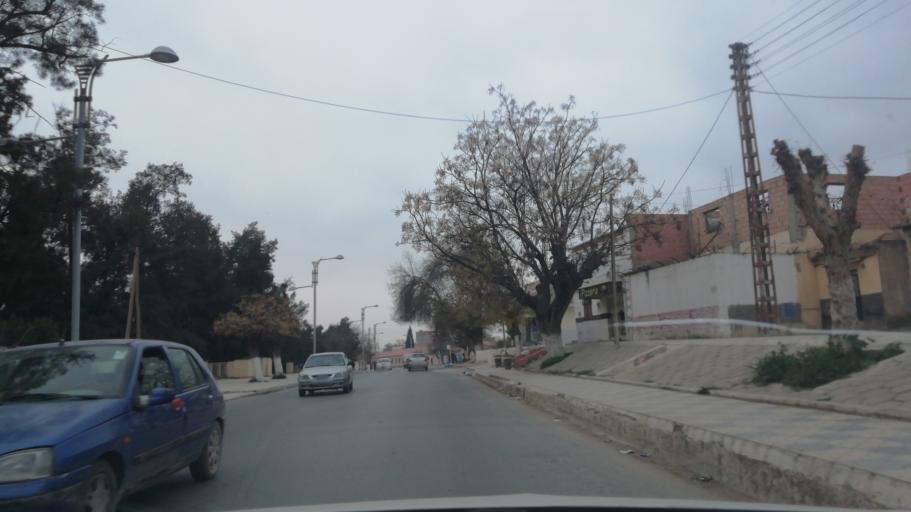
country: DZ
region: Sidi Bel Abbes
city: Sfizef
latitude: 35.2377
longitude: -0.2383
